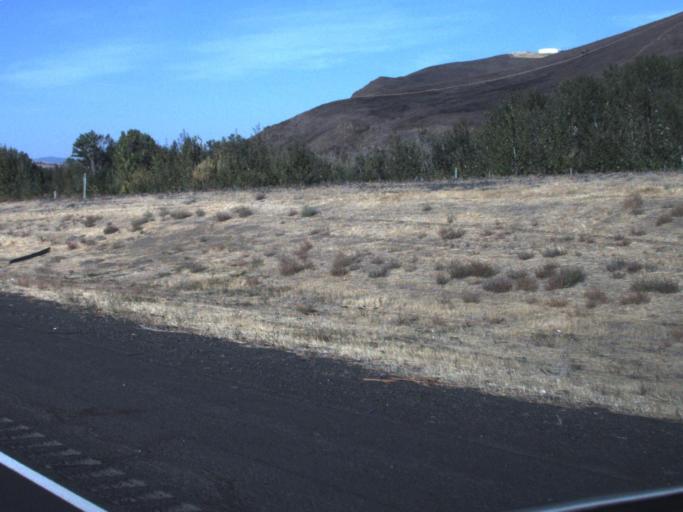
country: US
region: Washington
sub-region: Yakima County
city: Selah
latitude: 46.6233
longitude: -120.5342
